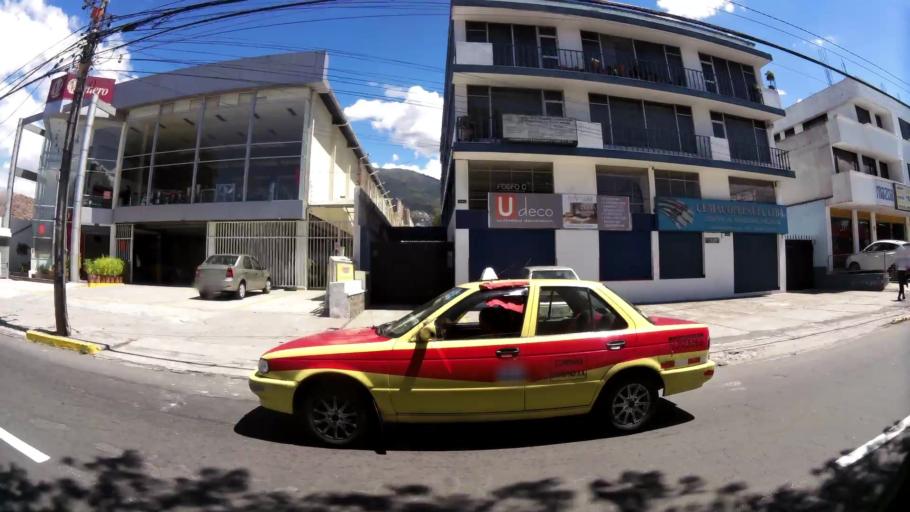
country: EC
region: Pichincha
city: Quito
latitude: -0.1624
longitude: -78.4860
